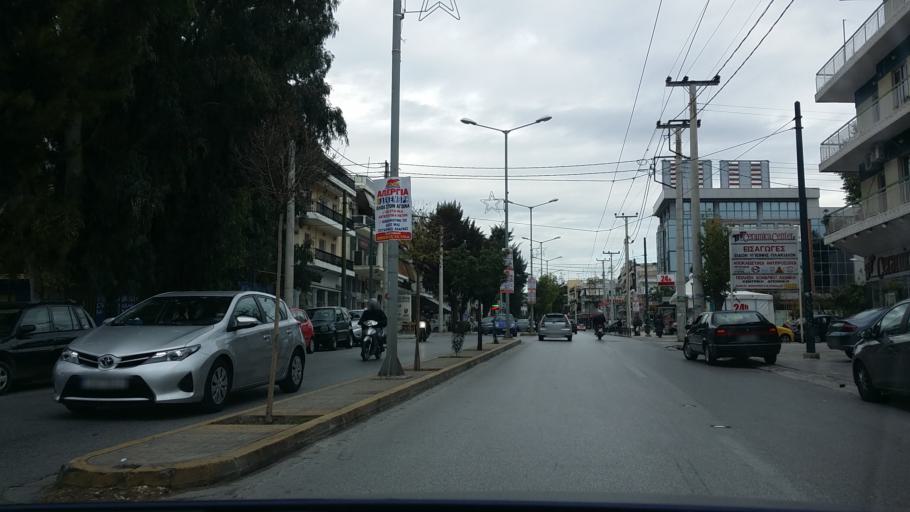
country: GR
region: Attica
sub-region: Nomarchia Athinas
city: Peristeri
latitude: 38.0179
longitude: 23.6924
